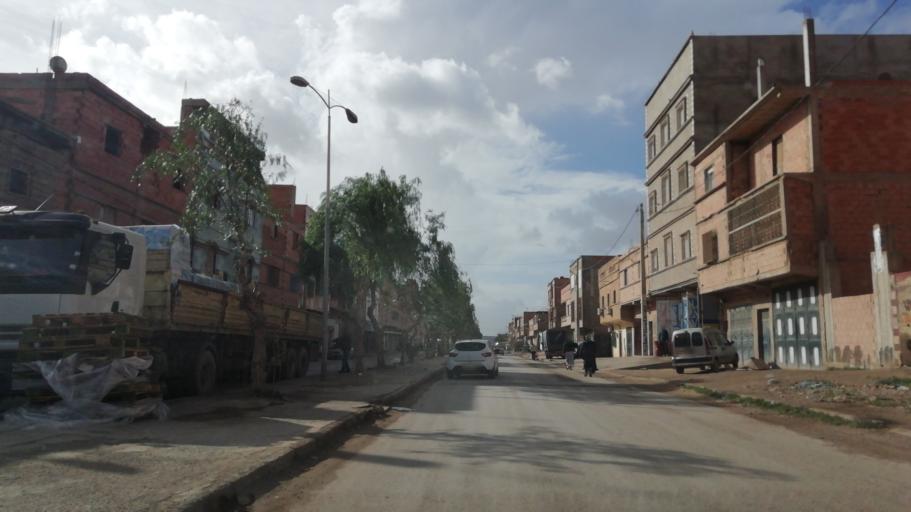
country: DZ
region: Oran
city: Es Senia
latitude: 35.6401
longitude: -0.5747
